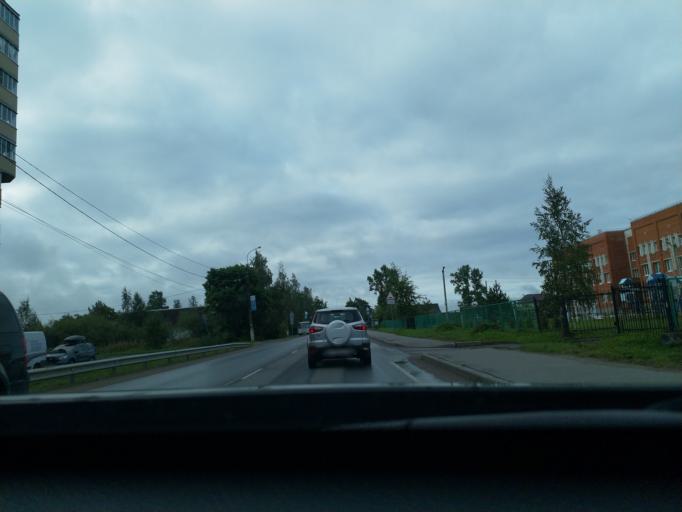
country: RU
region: Leningrad
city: Nikol'skoye
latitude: 59.6941
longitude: 30.7850
